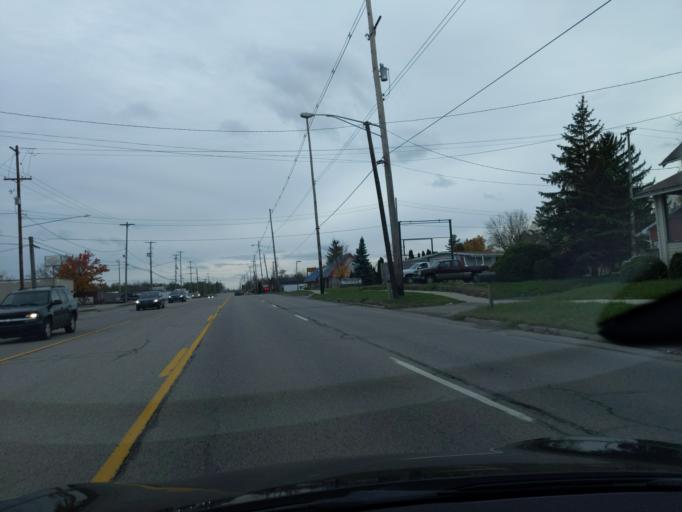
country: US
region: Michigan
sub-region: Ingham County
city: Lansing
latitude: 42.7797
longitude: -84.5428
